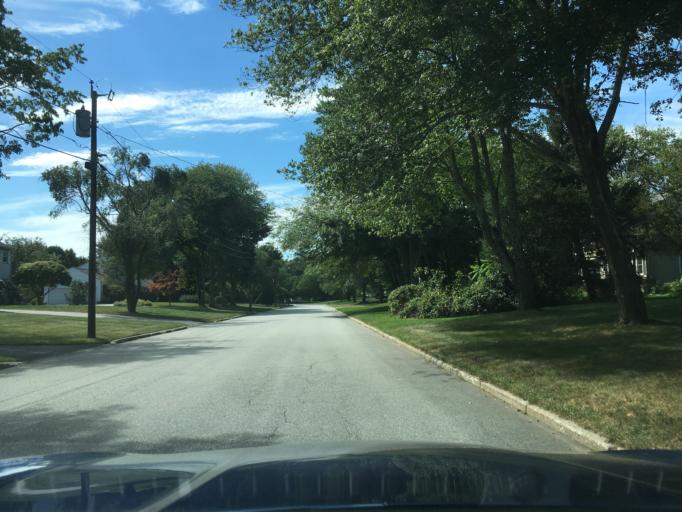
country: US
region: Rhode Island
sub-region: Kent County
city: East Greenwich
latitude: 41.6531
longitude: -71.4706
